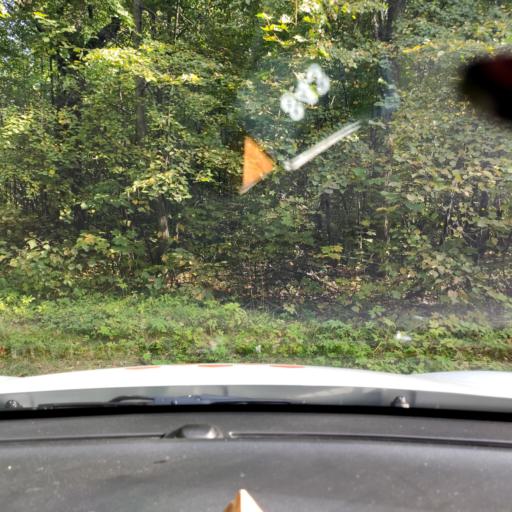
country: RU
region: Tatarstan
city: Staroye Arakchino
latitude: 55.8061
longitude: 49.0165
